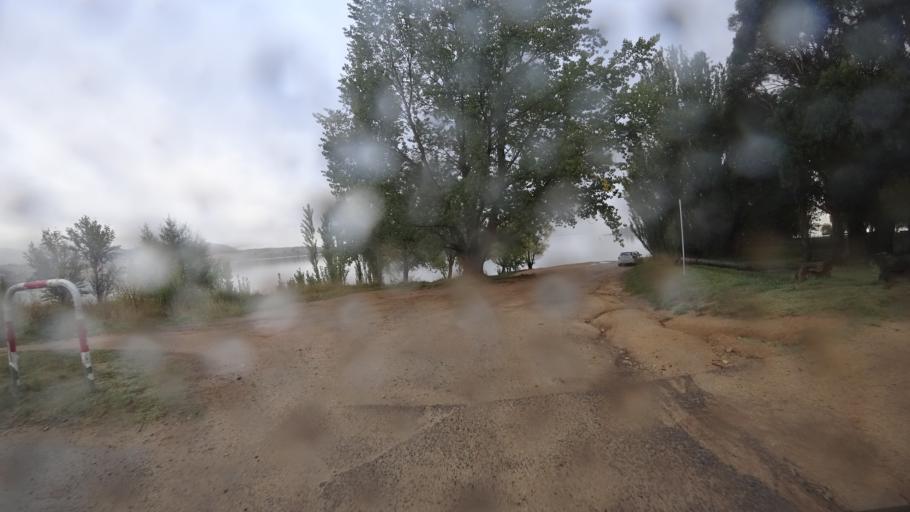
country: AU
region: New South Wales
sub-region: Snowy River
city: Jindabyne
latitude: -36.4137
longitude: 148.6111
